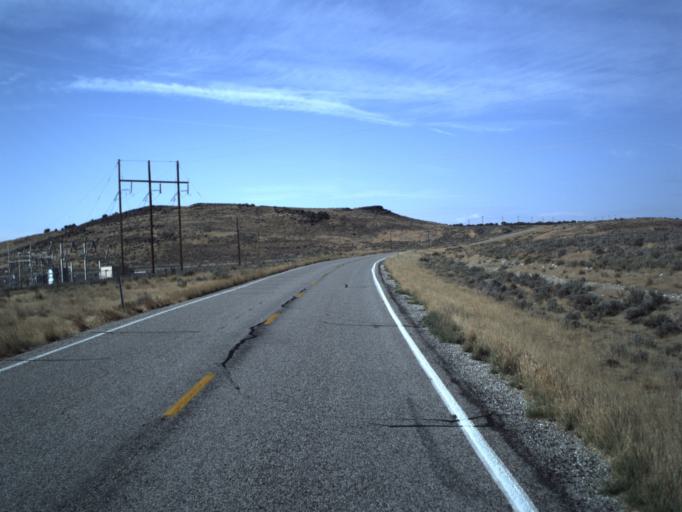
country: US
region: Idaho
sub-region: Minidoka County
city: Rupert
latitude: 41.8397
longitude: -113.1428
